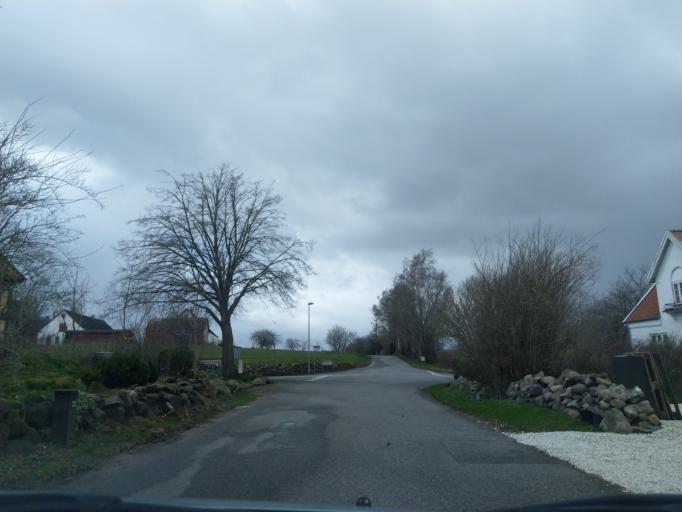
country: DK
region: Zealand
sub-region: Naestved Kommune
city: Fuglebjerg
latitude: 55.3525
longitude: 11.5781
